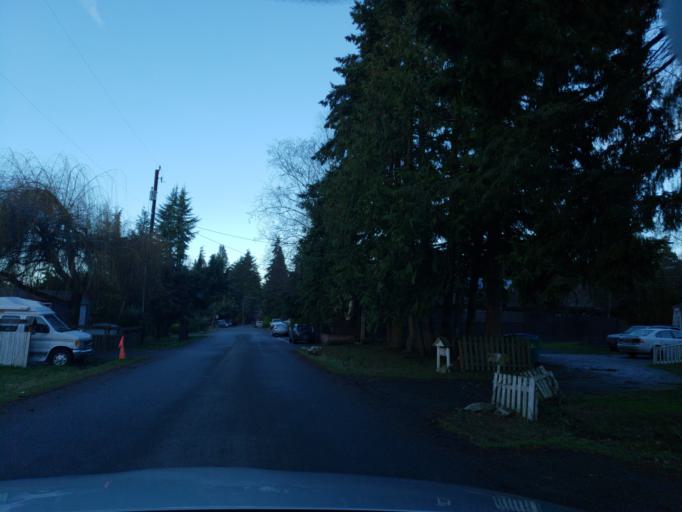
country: US
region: Washington
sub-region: King County
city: Shoreline
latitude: 47.7660
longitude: -122.3423
